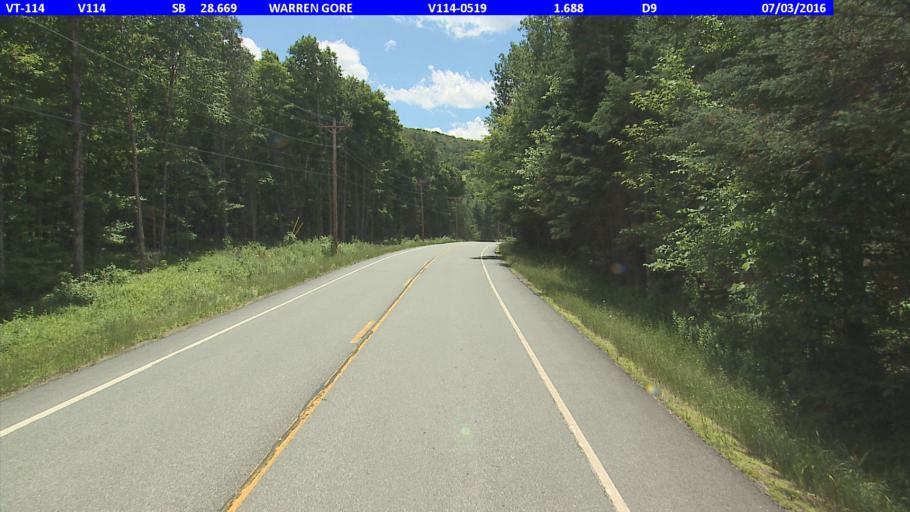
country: CA
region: Quebec
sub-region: Estrie
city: Coaticook
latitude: 44.9082
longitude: -71.8766
